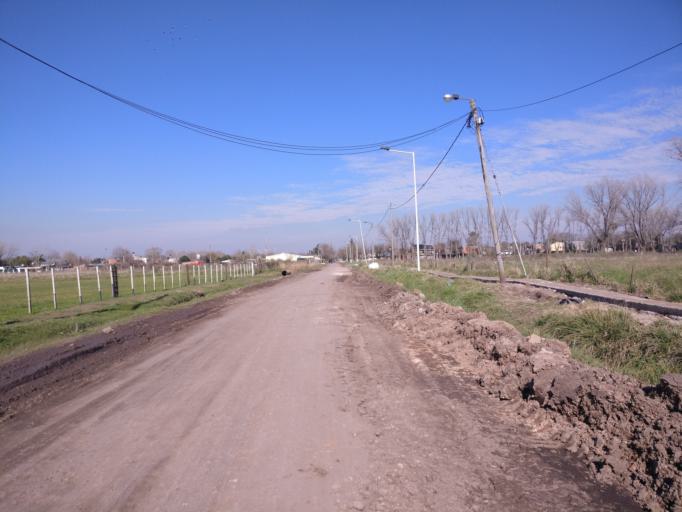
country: AR
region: Buenos Aires
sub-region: Partido de Ezeiza
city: Ezeiza
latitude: -34.9362
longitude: -58.6119
